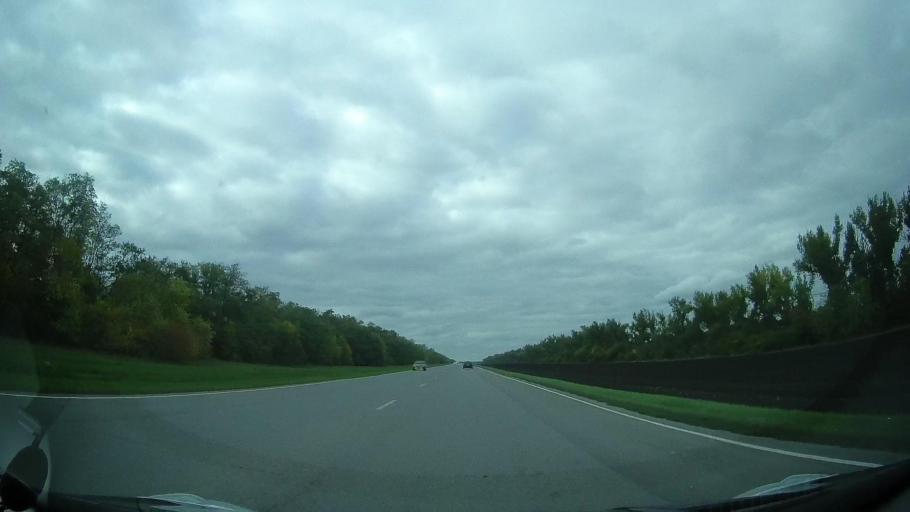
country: RU
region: Rostov
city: Yegorlykskaya
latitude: 46.6326
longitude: 40.5864
